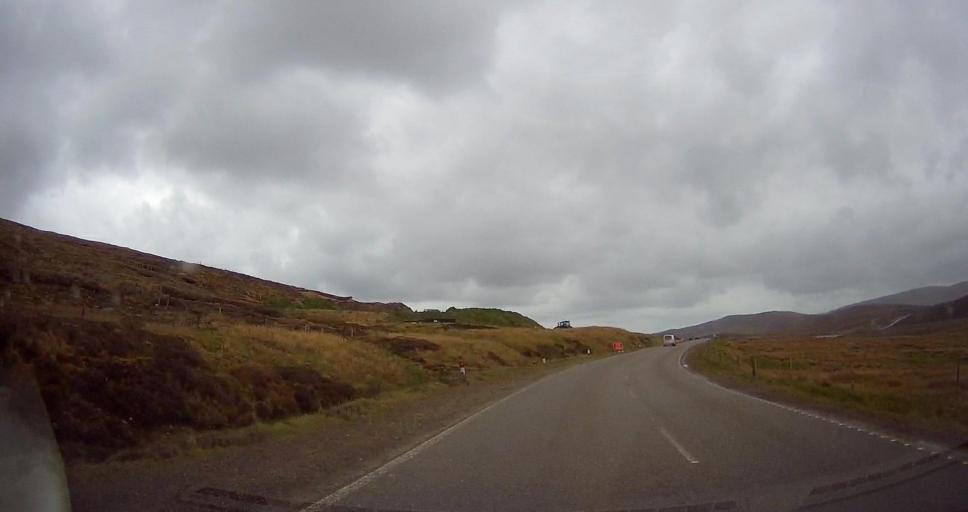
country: GB
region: Scotland
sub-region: Shetland Islands
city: Lerwick
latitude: 60.2873
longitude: -1.2413
